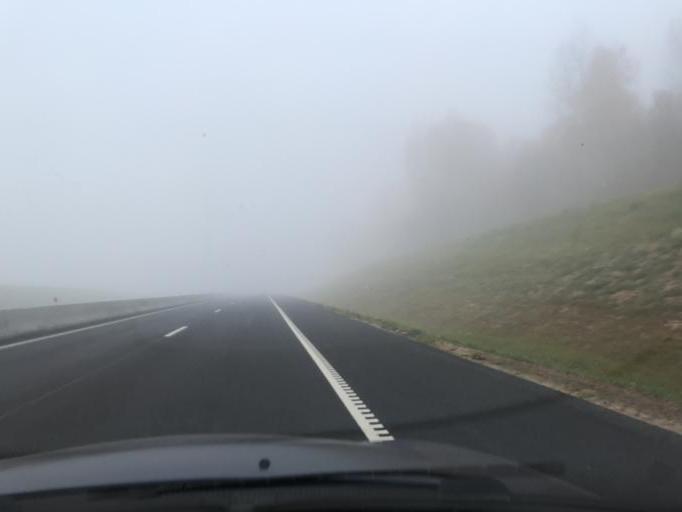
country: BY
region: Minsk
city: Valozhyn
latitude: 54.0396
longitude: 26.6612
